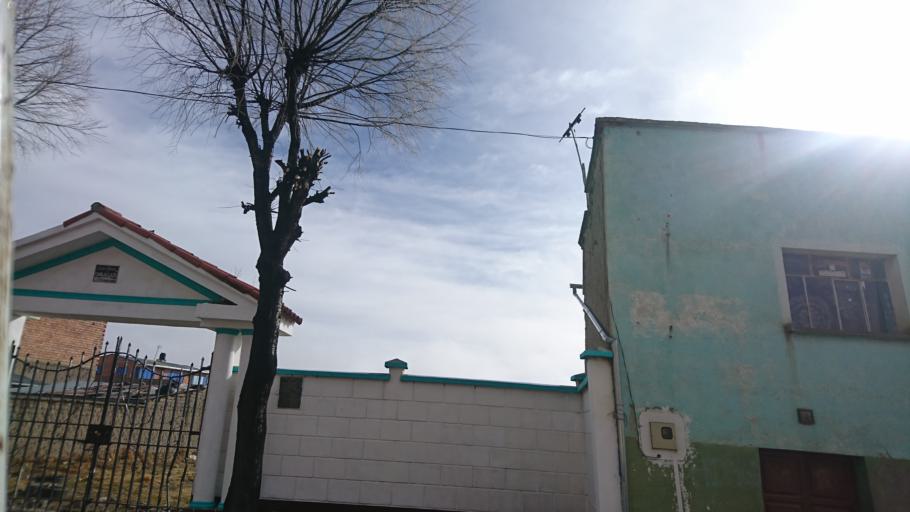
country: BO
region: La Paz
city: Batallas
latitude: -16.3993
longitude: -68.4749
